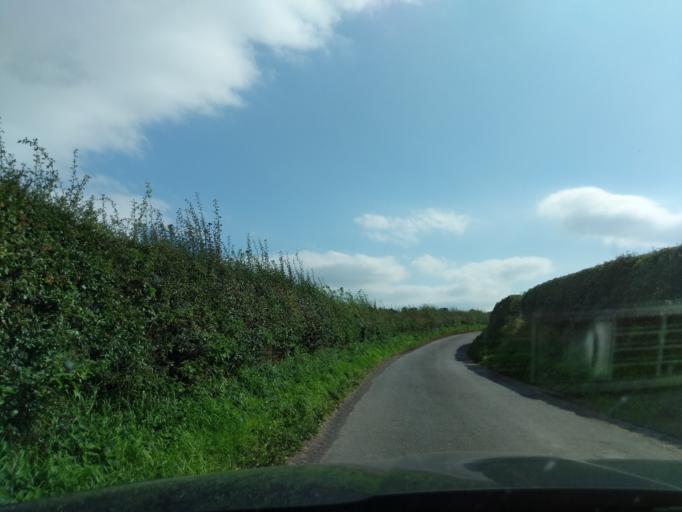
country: GB
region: England
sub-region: Northumberland
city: Ford
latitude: 55.6462
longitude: -2.1380
